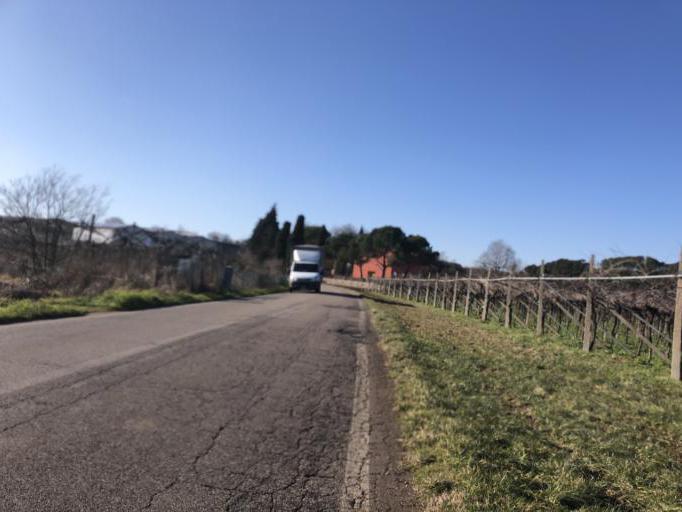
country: IT
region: Veneto
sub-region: Provincia di Verona
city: San Giorgio in Salici
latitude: 45.4340
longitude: 10.8014
